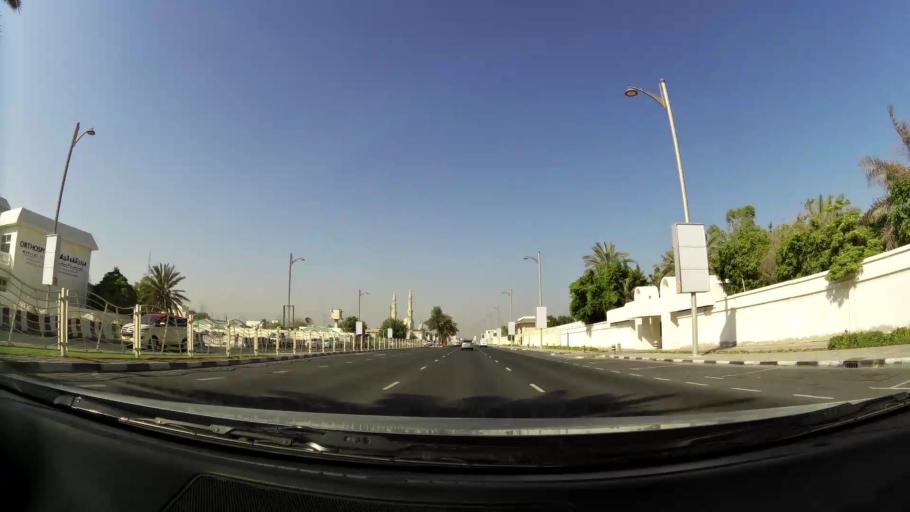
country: AE
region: Ash Shariqah
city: Sharjah
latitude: 25.2375
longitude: 55.2674
